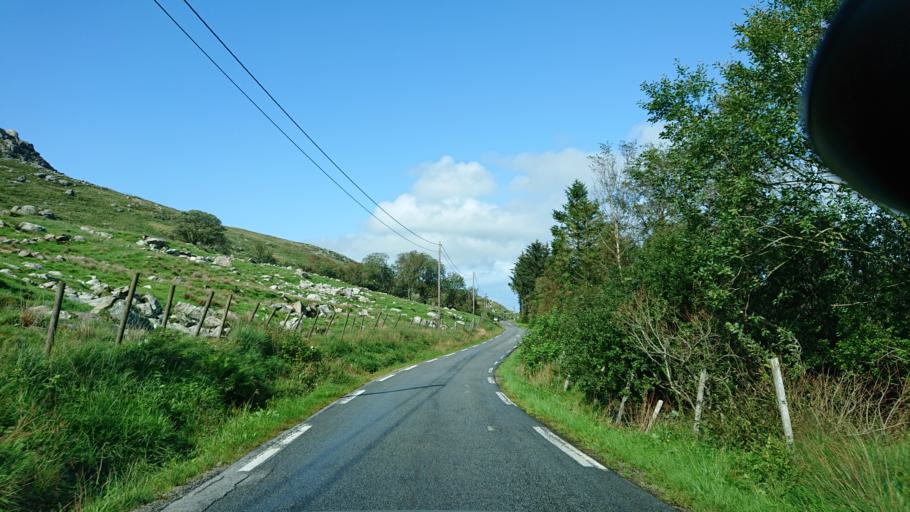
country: NO
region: Rogaland
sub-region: Gjesdal
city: Algard
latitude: 58.6994
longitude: 5.8897
